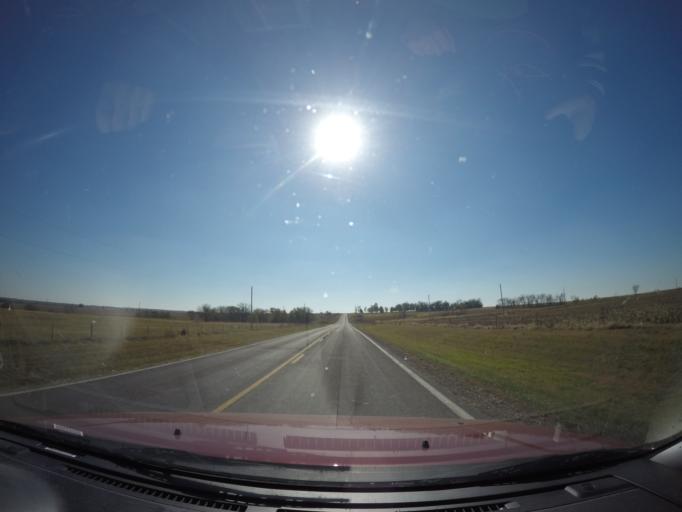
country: US
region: Kansas
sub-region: Morris County
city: Council Grove
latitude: 38.7695
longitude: -96.5012
